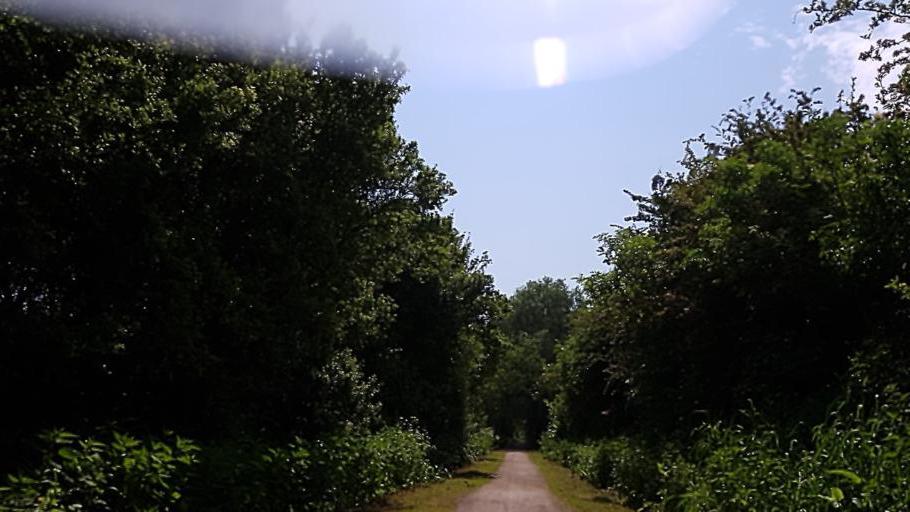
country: BE
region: Wallonia
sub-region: Province du Hainaut
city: Peruwelz
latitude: 50.4918
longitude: 3.5686
